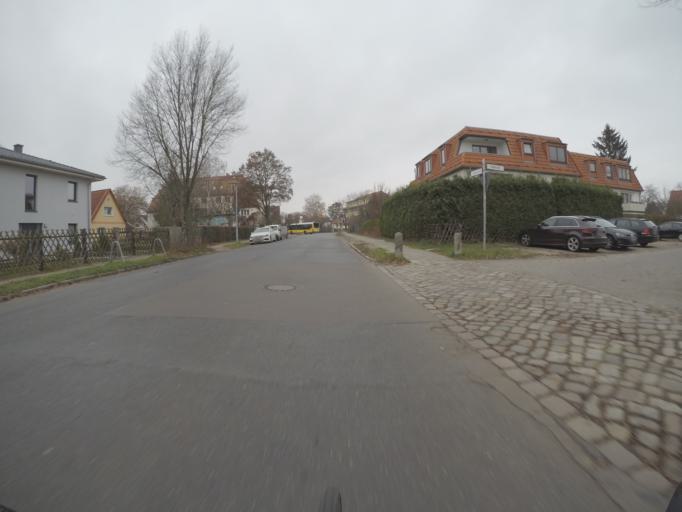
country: DE
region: Berlin
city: Biesdorf
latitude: 52.4870
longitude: 13.5761
